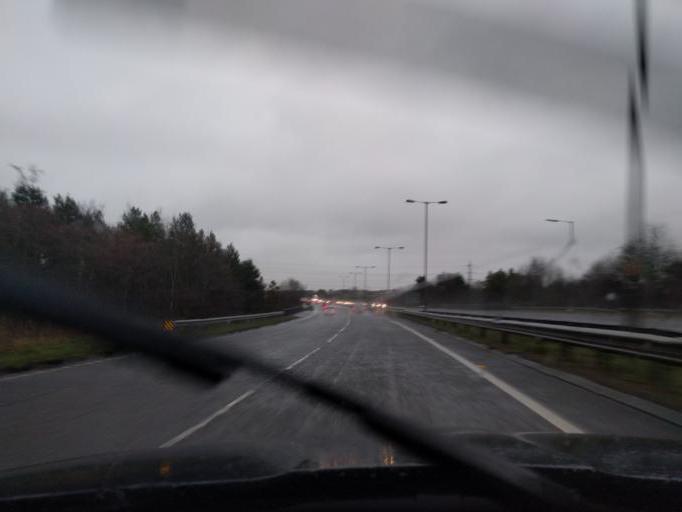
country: GB
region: England
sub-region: Northumberland
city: Bedlington
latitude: 55.1367
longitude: -1.5595
